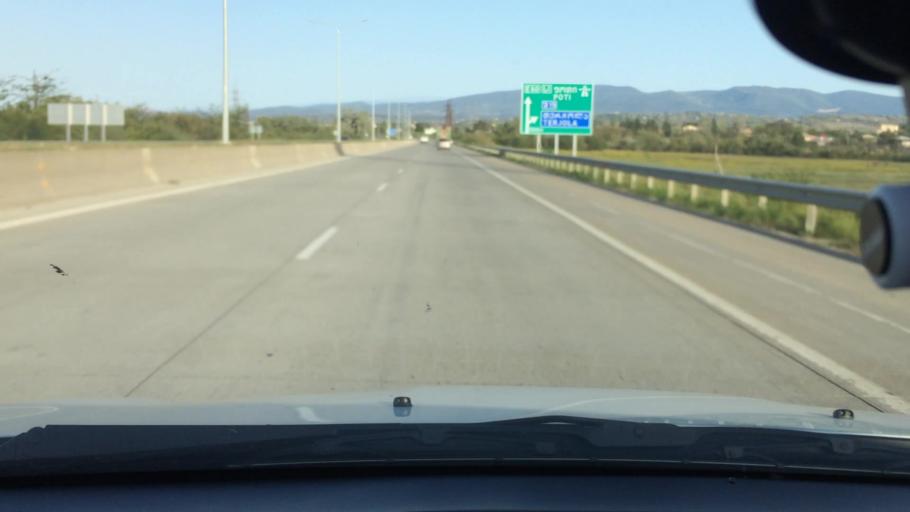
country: GE
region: Imereti
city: Zestap'oni
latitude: 42.1508
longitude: 42.9607
